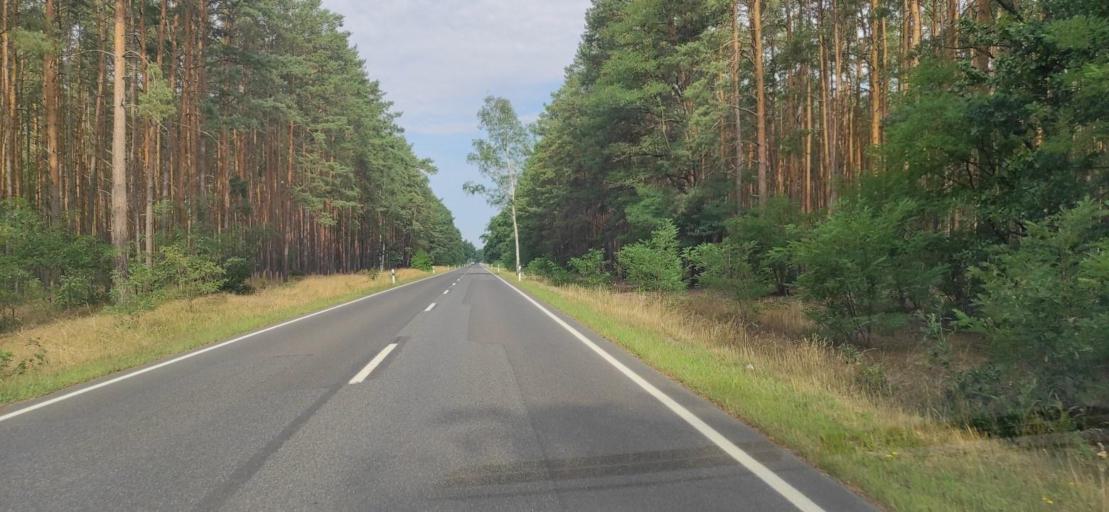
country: DE
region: Brandenburg
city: Forst
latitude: 51.6974
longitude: 14.7028
